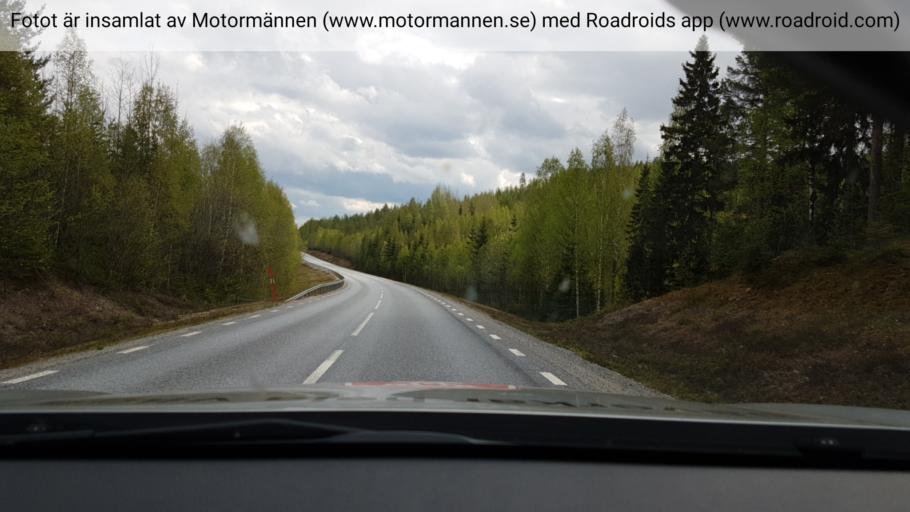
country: SE
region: Vaesterbotten
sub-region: Lycksele Kommun
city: Lycksele
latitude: 64.0420
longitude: 18.5818
